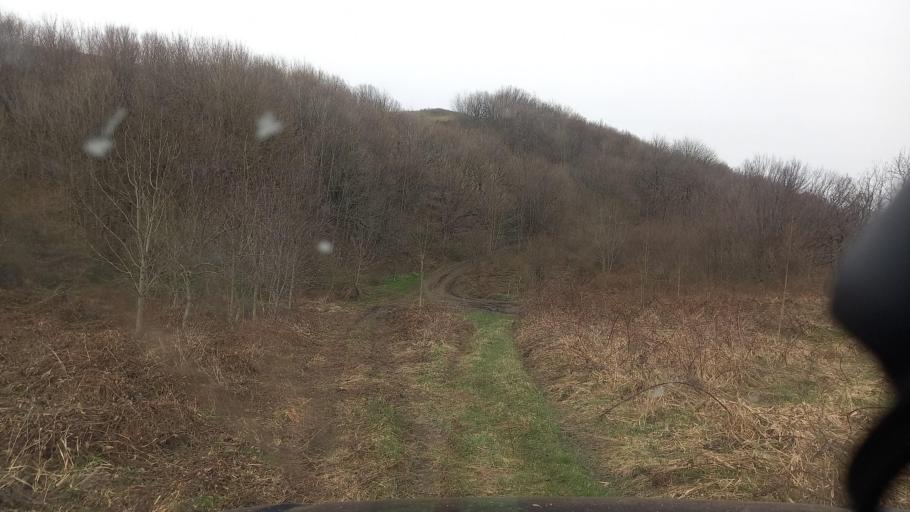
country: RU
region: Krasnodarskiy
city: Gelendzhik
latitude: 44.6155
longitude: 38.2110
